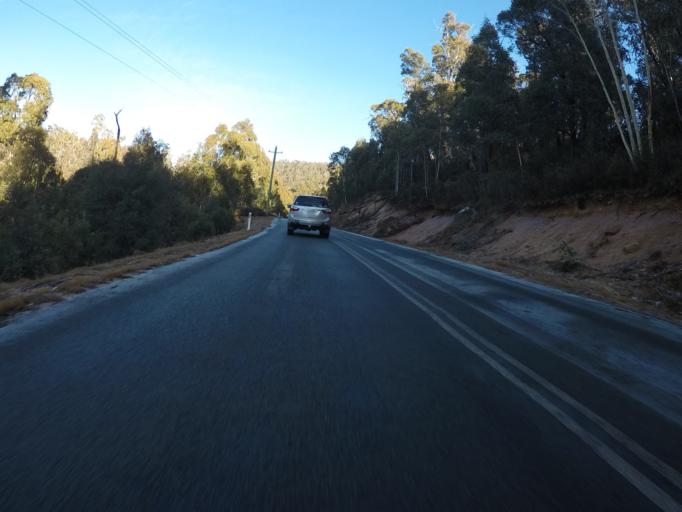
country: AU
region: Australian Capital Territory
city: Macarthur
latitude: -35.4921
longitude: 148.9284
